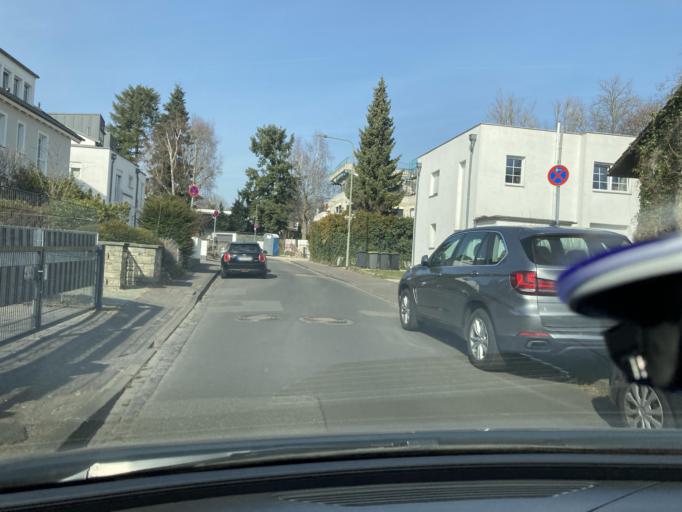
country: DE
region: Hesse
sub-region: Regierungsbezirk Darmstadt
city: Steinbach am Taunus
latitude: 50.1563
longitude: 8.6280
